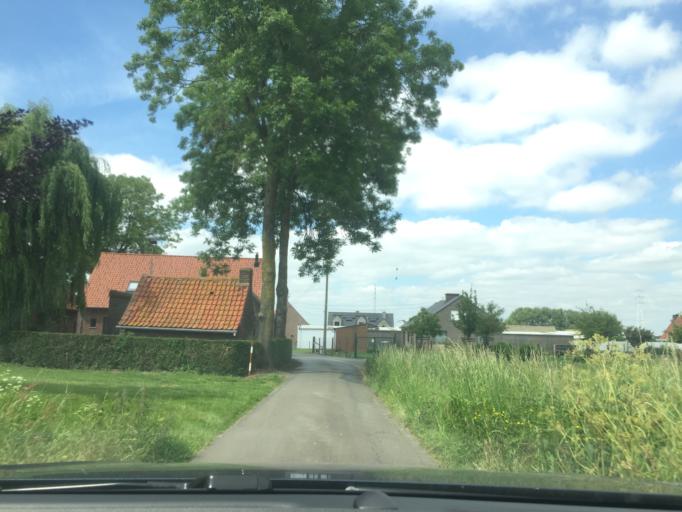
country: BE
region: Flanders
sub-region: Provincie West-Vlaanderen
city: Izegem
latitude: 50.8962
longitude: 3.2175
